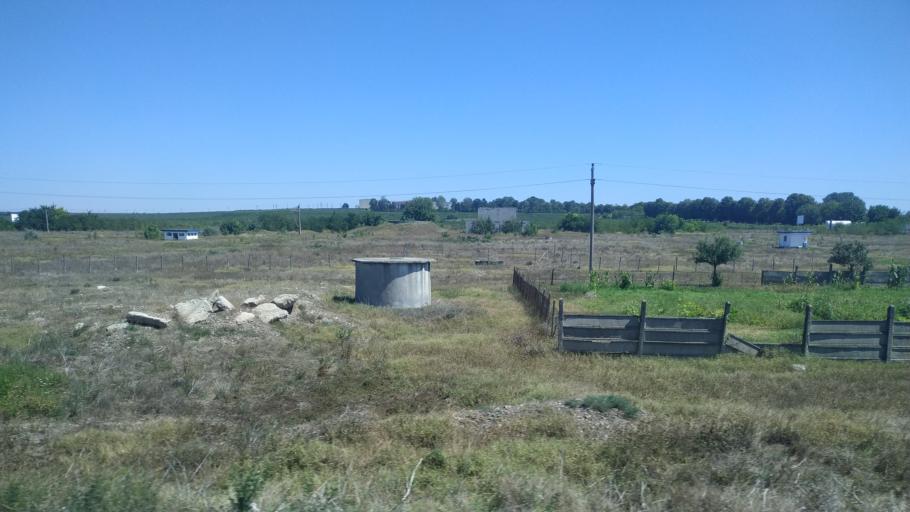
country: RO
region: Constanta
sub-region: Oras Murfatlar
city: Murfatlar
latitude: 44.1817
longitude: 28.3986
